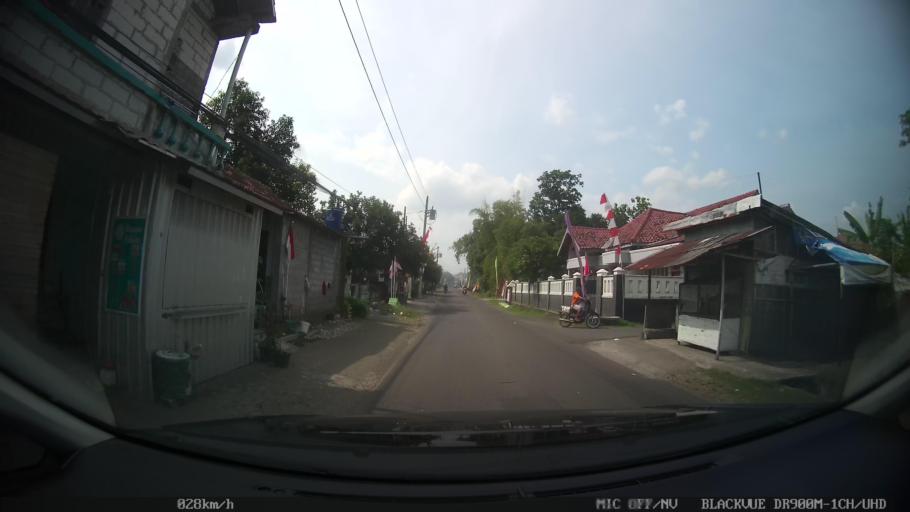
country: ID
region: Daerah Istimewa Yogyakarta
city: Depok
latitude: -7.7947
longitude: 110.4457
